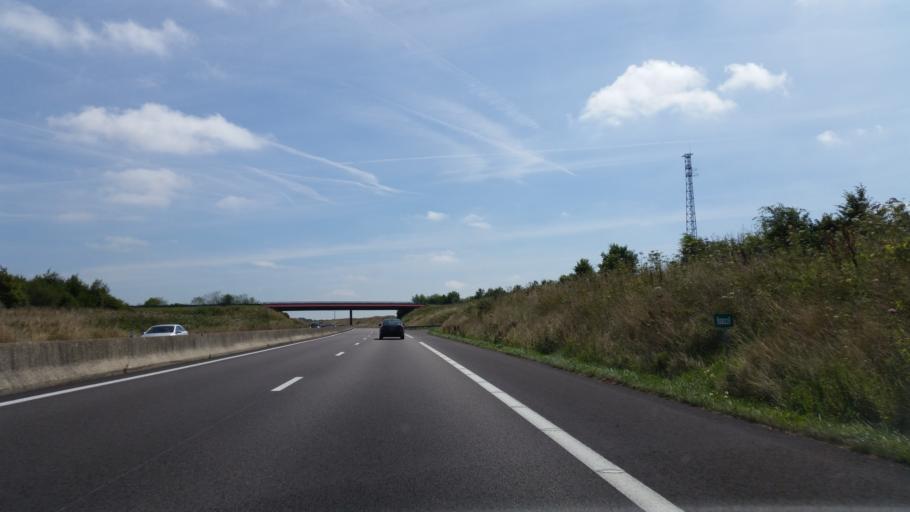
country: FR
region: Haute-Normandie
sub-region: Departement de la Seine-Maritime
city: Gaillefontaine
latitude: 49.7394
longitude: 1.6073
